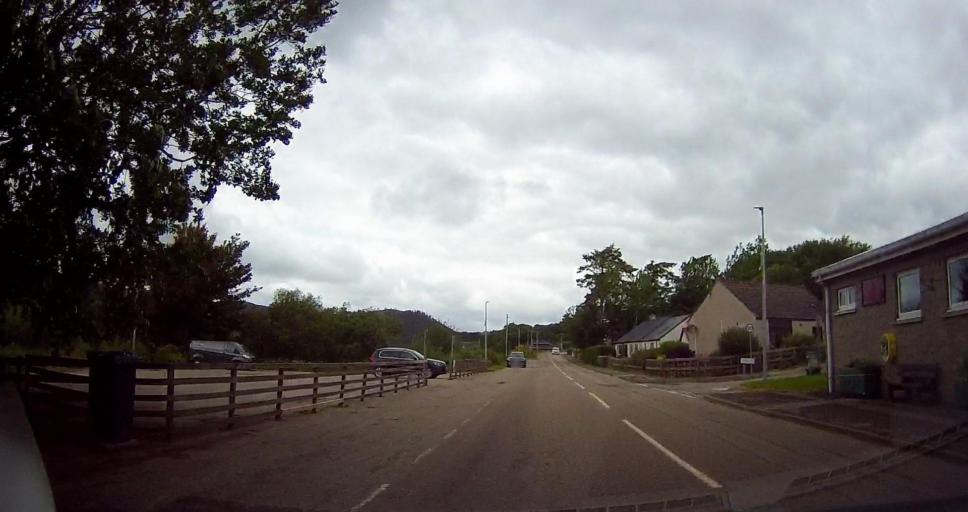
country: GB
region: Scotland
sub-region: Highland
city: Dornoch
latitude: 57.9864
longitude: -4.1527
